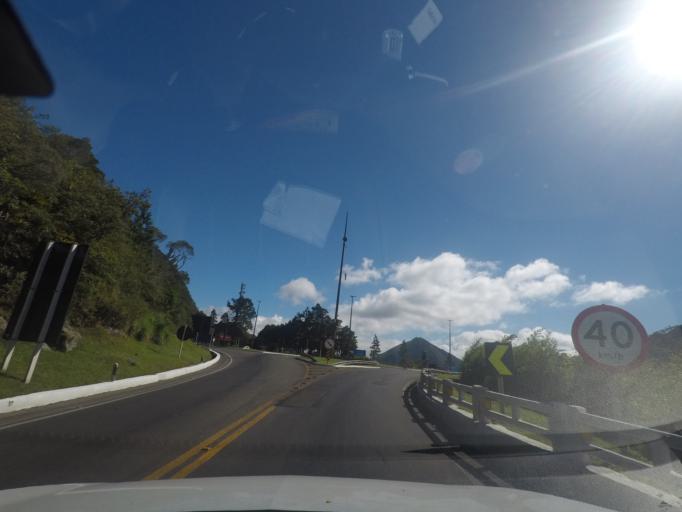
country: BR
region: Rio de Janeiro
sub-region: Teresopolis
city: Teresopolis
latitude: -22.4629
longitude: -42.9881
